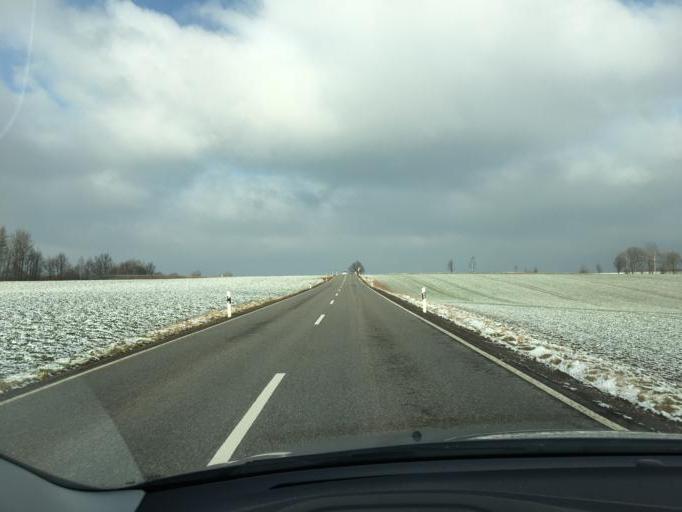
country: DE
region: Saxony
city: Narsdorf
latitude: 50.9787
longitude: 12.6983
